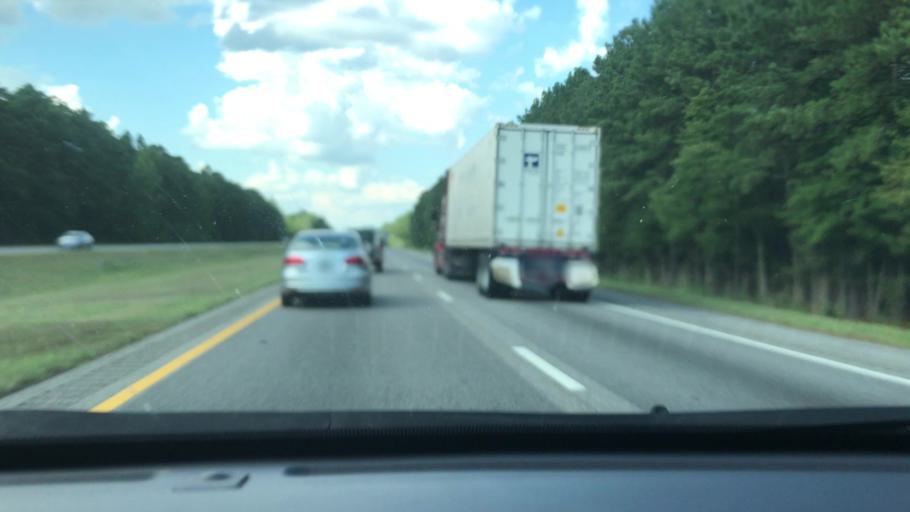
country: US
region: South Carolina
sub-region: Florence County
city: Timmonsville
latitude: 33.9974
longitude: -80.0098
